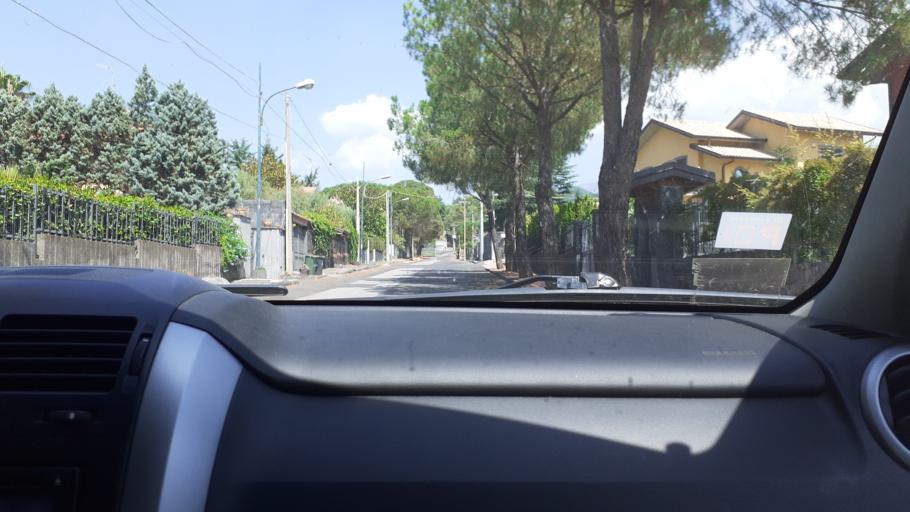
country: IT
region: Sicily
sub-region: Catania
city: Nicolosi
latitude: 37.6228
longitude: 15.0263
